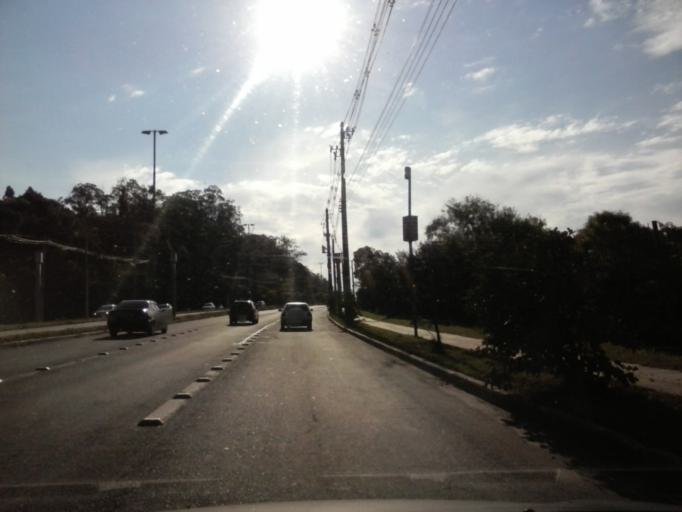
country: BR
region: Rio Grande do Sul
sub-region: Porto Alegre
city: Porto Alegre
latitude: -30.0741
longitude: -51.1364
